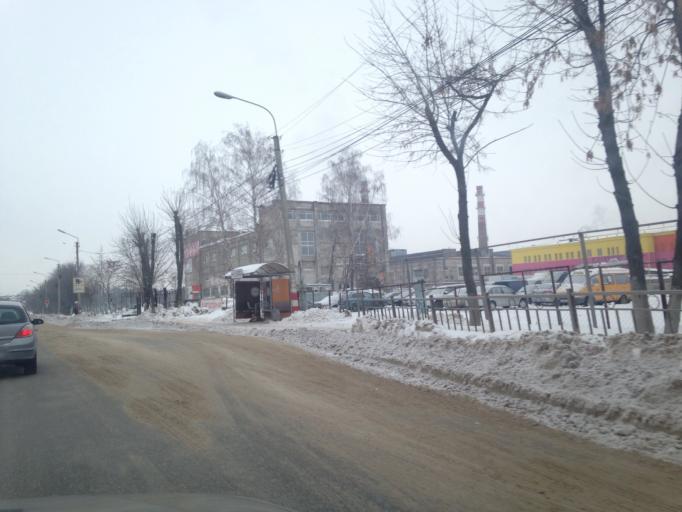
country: RU
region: Ulyanovsk
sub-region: Ulyanovskiy Rayon
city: Ulyanovsk
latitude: 54.2979
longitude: 48.3298
